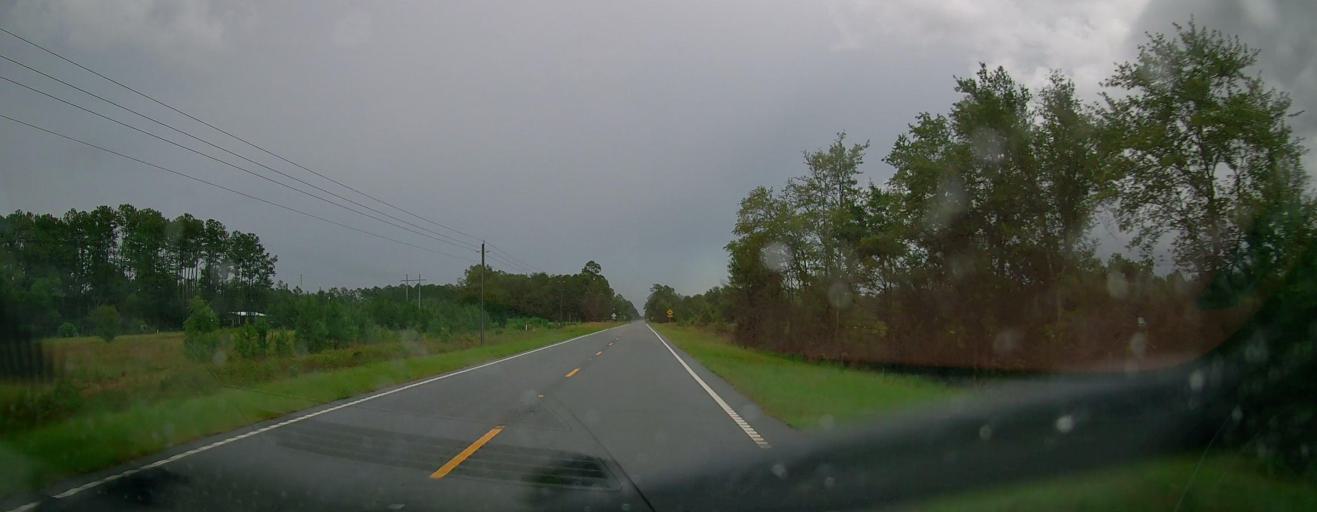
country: US
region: Georgia
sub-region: Brantley County
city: Nahunta
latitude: 31.3382
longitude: -81.9666
